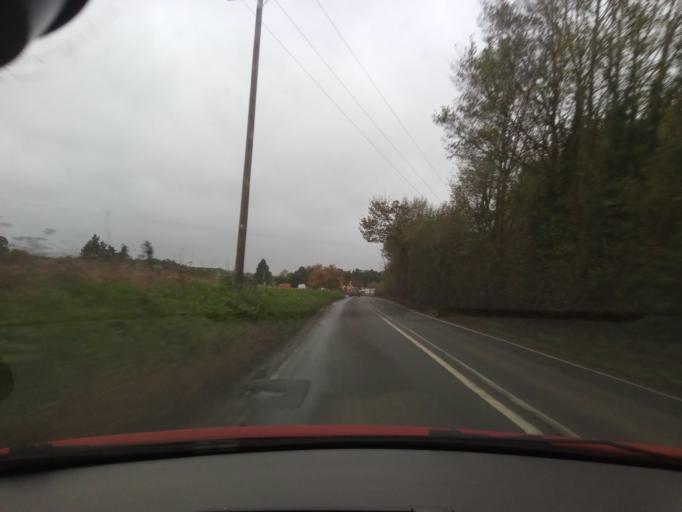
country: GB
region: England
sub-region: Suffolk
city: Kedington
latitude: 52.0574
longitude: 0.5112
